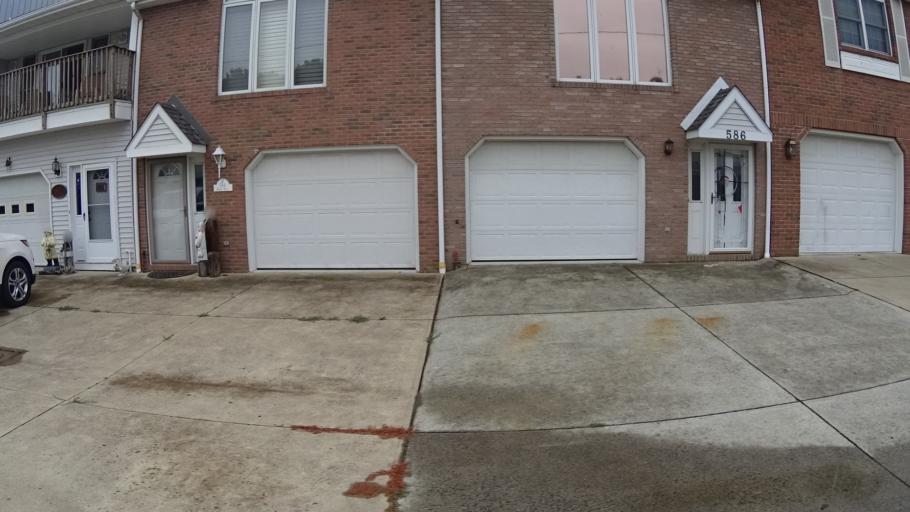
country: US
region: Ohio
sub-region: Erie County
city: Sandusky
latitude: 41.4519
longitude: -82.6790
